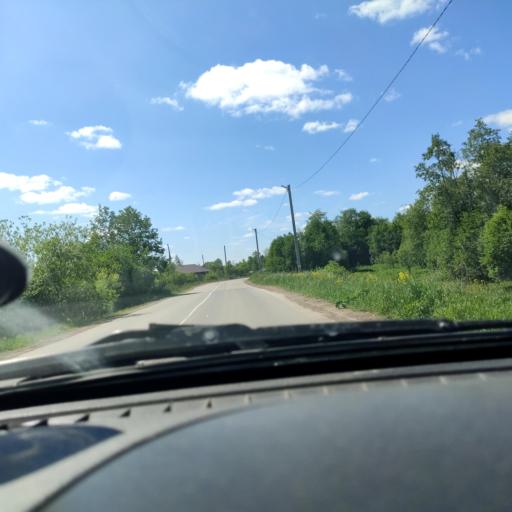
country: RU
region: Perm
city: Kukushtan
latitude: 57.6491
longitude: 56.5193
